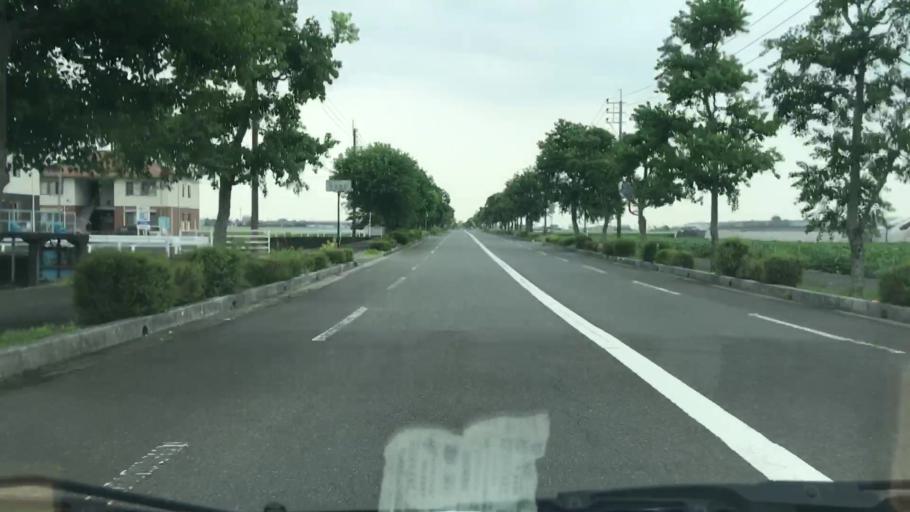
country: JP
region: Saga Prefecture
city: Saga-shi
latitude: 33.2070
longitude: 130.3036
